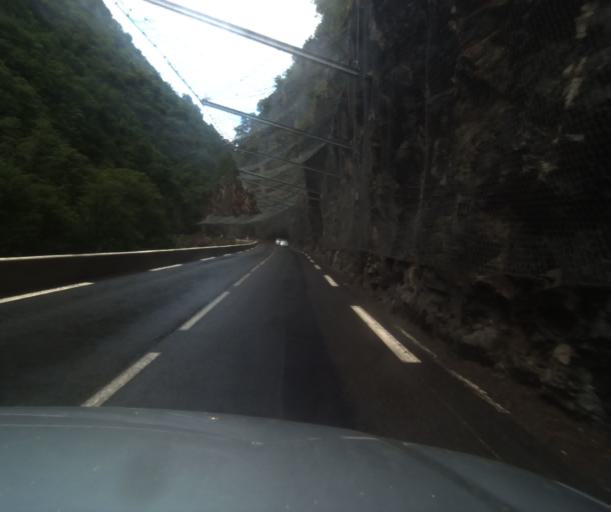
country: FR
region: Midi-Pyrenees
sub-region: Departement des Hautes-Pyrenees
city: Pierrefitte-Nestalas
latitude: 42.9335
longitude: -0.0469
